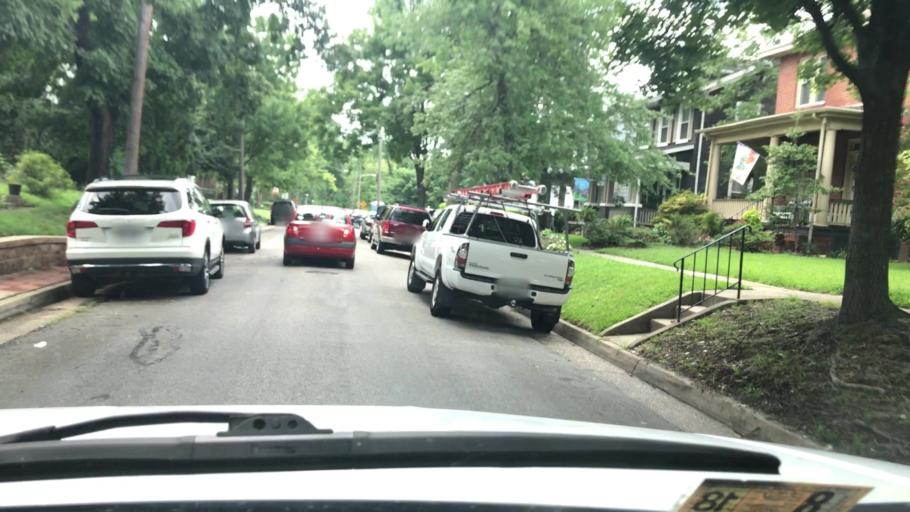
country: US
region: Virginia
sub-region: City of Richmond
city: Richmond
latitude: 37.5697
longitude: -77.4399
